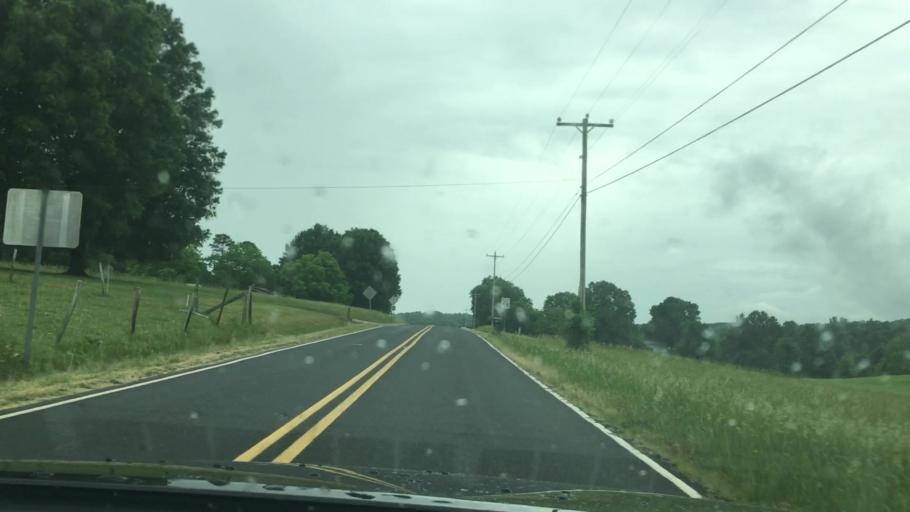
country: US
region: North Carolina
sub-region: Stanly County
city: Badin
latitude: 35.3725
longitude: -80.1170
